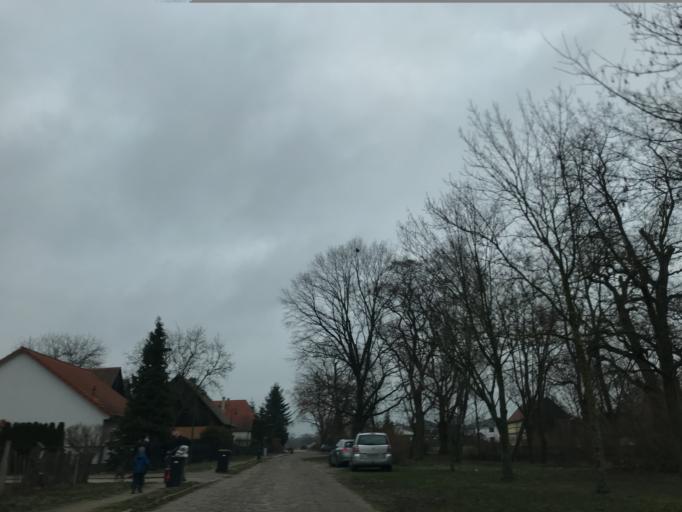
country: DE
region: Brandenburg
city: Wustermark
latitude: 52.5901
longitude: 12.9269
